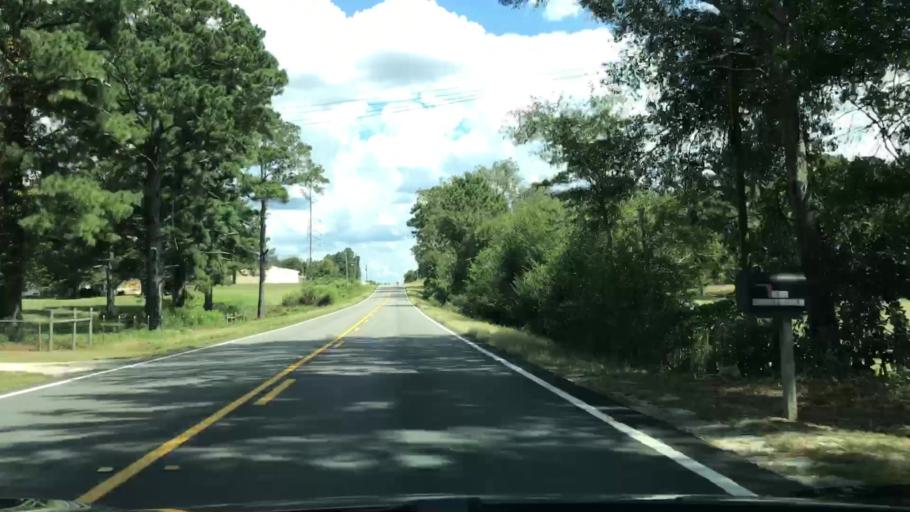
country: US
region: Georgia
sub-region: Greene County
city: Greensboro
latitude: 33.5663
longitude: -83.1549
